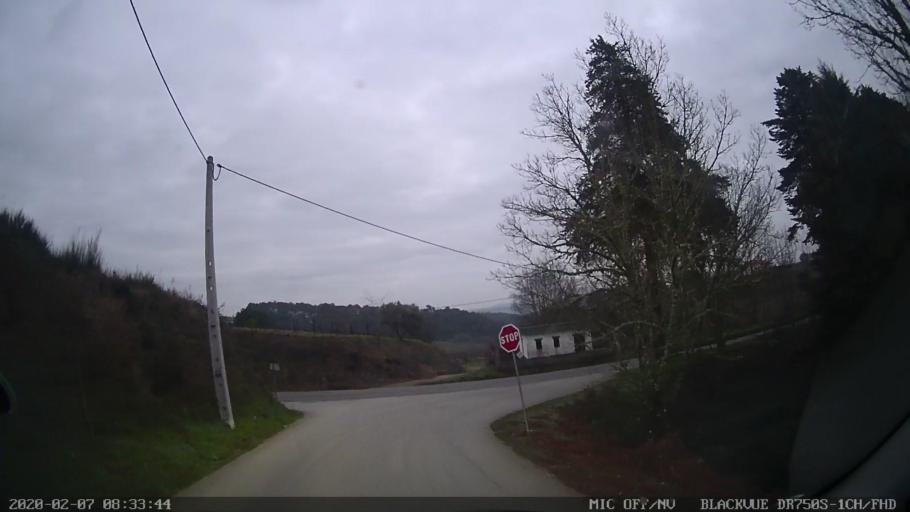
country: PT
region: Vila Real
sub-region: Sabrosa
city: Sabrosa
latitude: 41.2560
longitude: -7.5841
